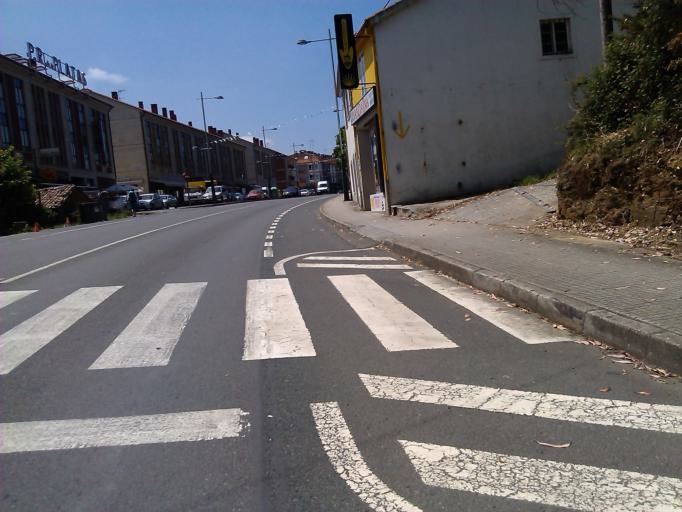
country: ES
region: Galicia
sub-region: Provincia da Coruna
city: Touro
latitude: 42.9073
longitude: -8.3593
